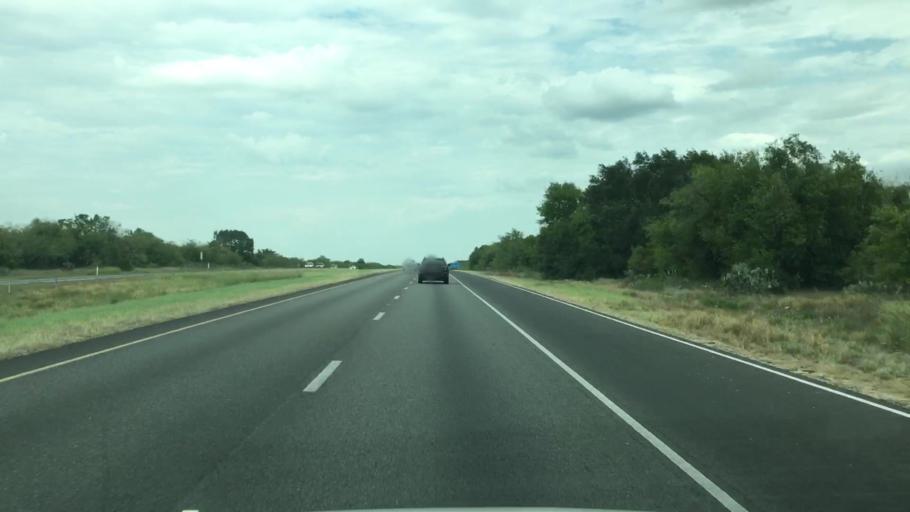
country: US
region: Texas
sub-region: Atascosa County
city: Poteet
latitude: 29.1253
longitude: -98.4306
